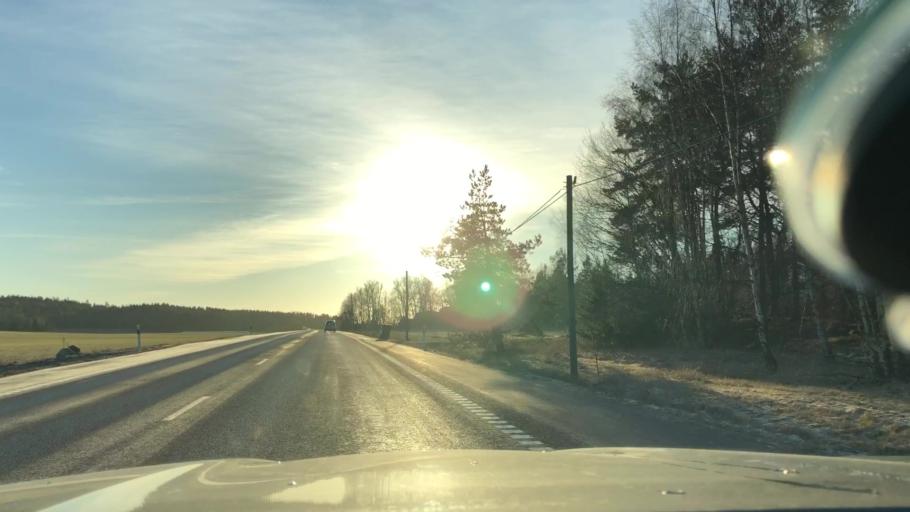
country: SE
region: Soedermanland
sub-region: Trosa Kommun
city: Vagnharad
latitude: 59.0321
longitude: 17.5968
